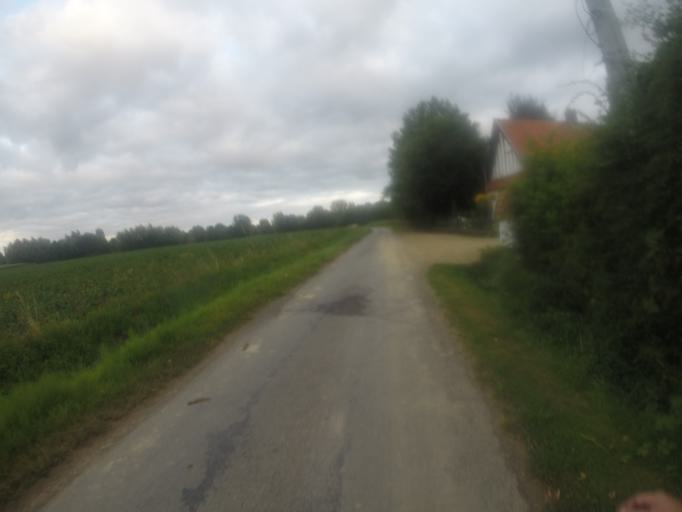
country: BE
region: Flanders
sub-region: Provincie West-Vlaanderen
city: Poperinge
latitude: 50.8465
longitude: 2.7056
